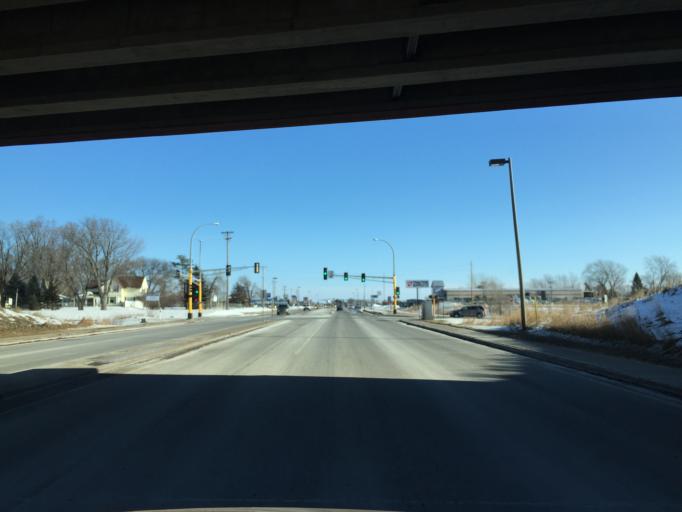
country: US
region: Minnesota
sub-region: Isanti County
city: Cambridge
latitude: 45.5727
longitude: -93.2102
